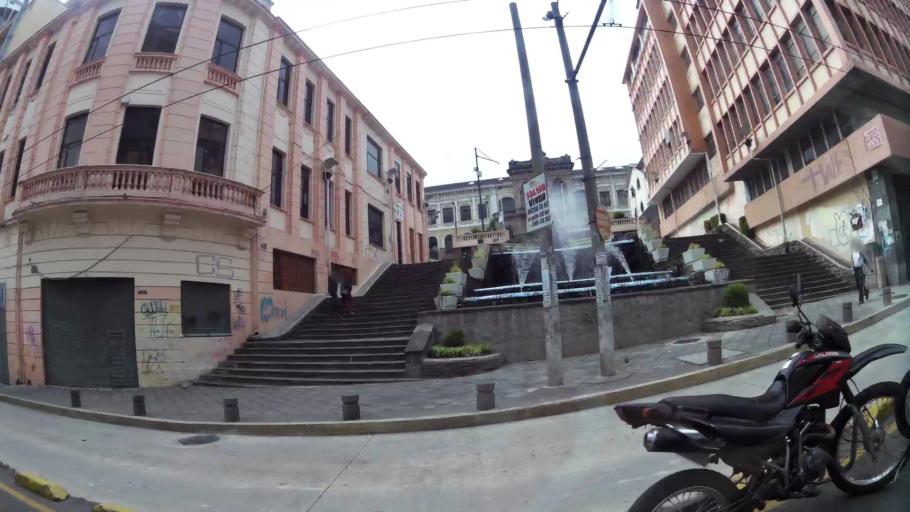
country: EC
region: Pichincha
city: Quito
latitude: -0.2124
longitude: -78.5020
